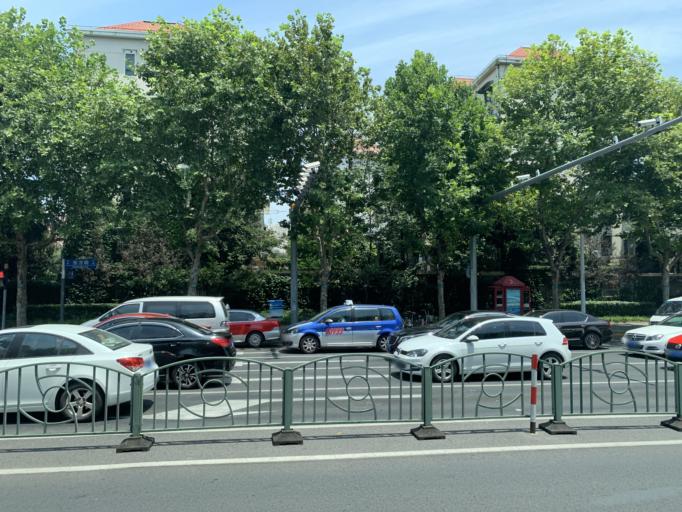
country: CN
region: Shanghai Shi
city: Pudong
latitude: 31.2373
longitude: 121.5179
